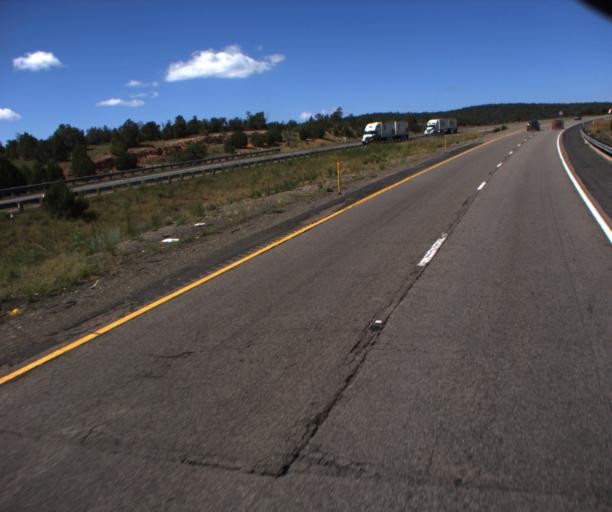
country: US
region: Arizona
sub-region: Mohave County
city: Peach Springs
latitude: 35.2936
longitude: -113.0317
